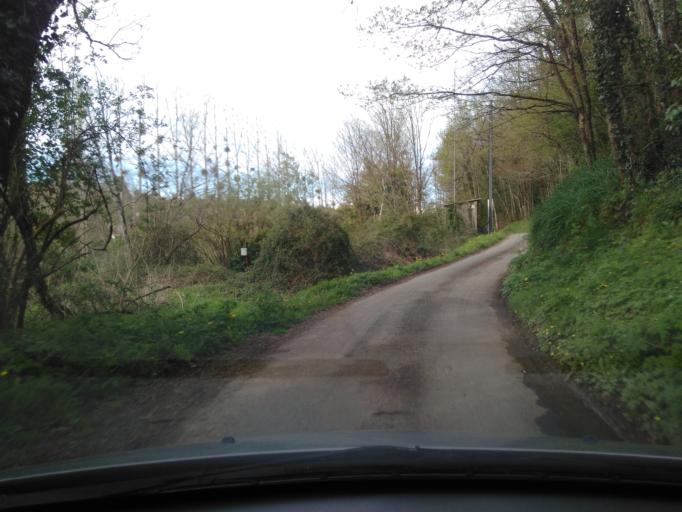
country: FR
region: Pays de la Loire
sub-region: Departement de la Vendee
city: Chantonnay
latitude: 46.6272
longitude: -1.0783
